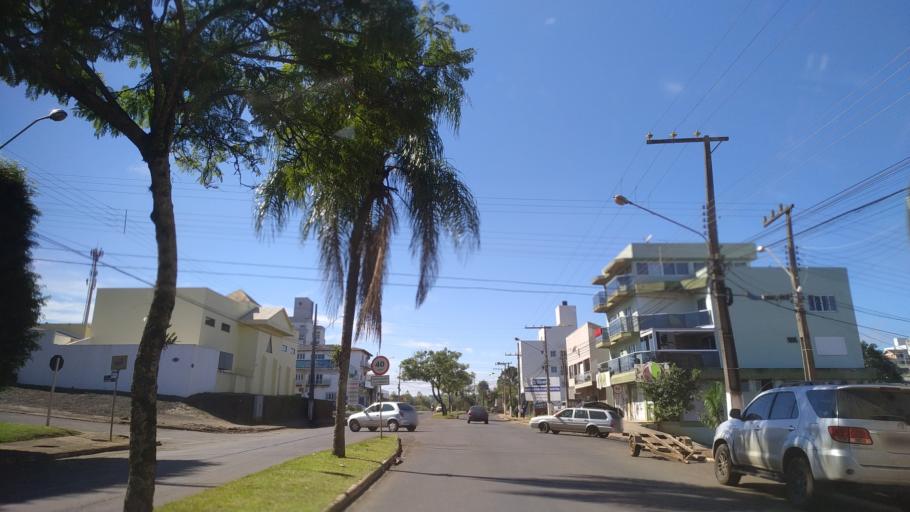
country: BR
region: Santa Catarina
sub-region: Chapeco
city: Chapeco
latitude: -27.1052
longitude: -52.6018
